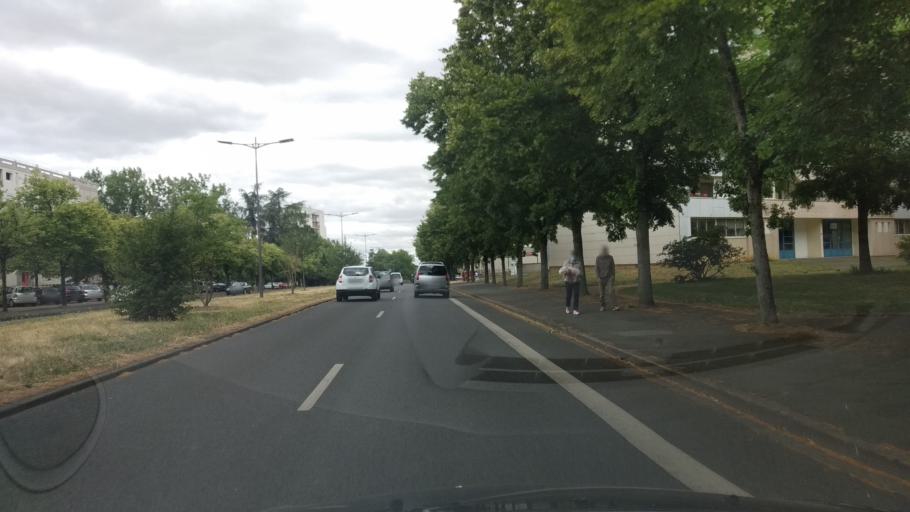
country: FR
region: Poitou-Charentes
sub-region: Departement de la Vienne
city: Poitiers
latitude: 46.5905
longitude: 0.3539
